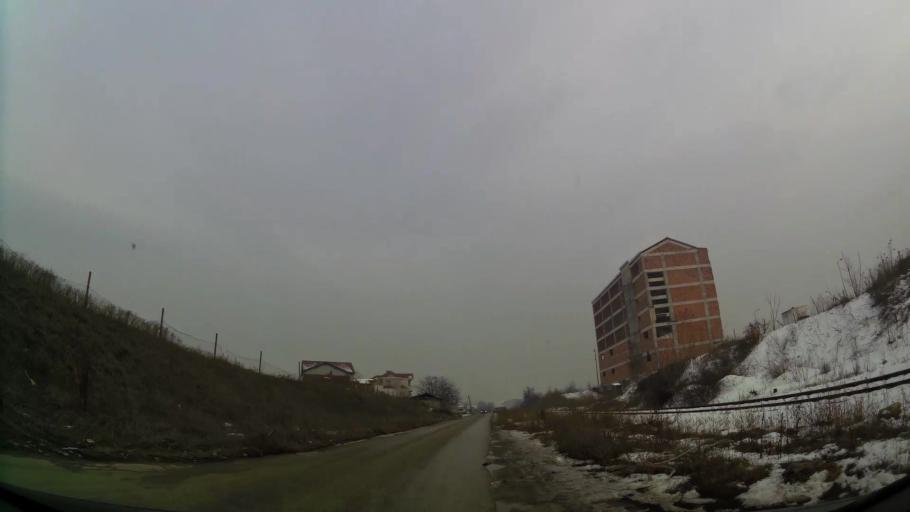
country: MK
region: Suto Orizari
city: Suto Orizare
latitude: 42.0278
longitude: 21.4216
